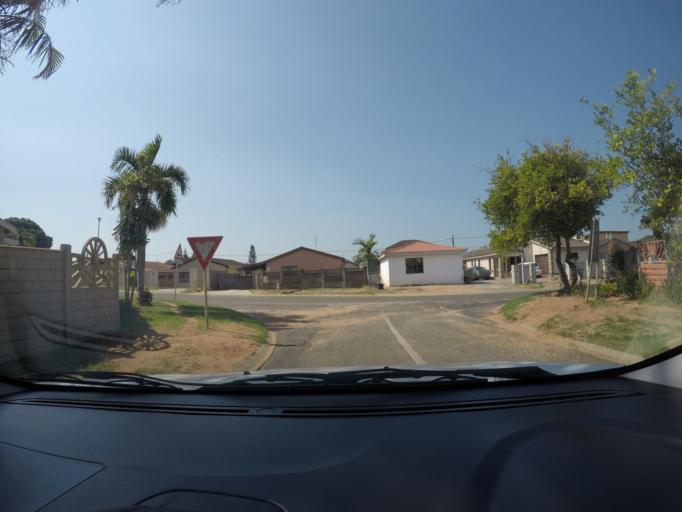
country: ZA
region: KwaZulu-Natal
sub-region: uThungulu District Municipality
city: Richards Bay
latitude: -28.7209
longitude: 32.0445
